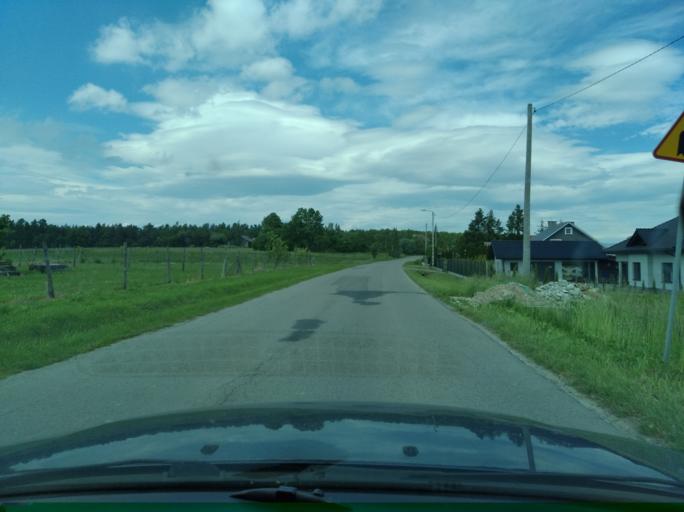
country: PL
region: Subcarpathian Voivodeship
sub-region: Powiat ropczycko-sedziszowski
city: Ropczyce
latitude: 49.9999
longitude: 21.6133
